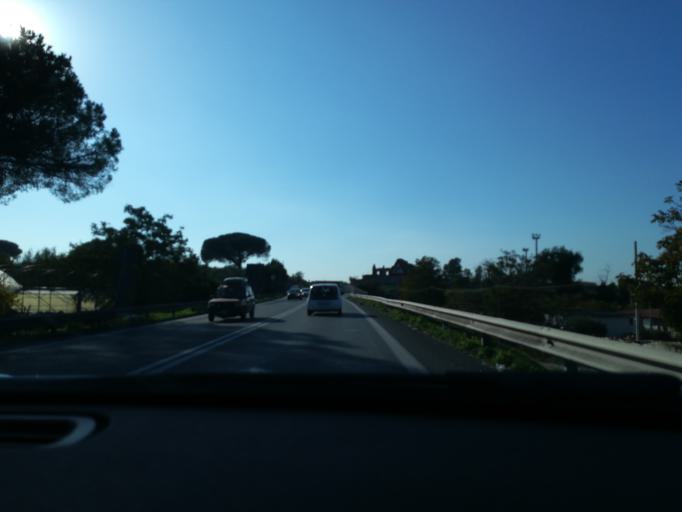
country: IT
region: Campania
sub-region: Provincia di Napoli
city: Sant'Anastasia
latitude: 40.8767
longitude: 14.3912
